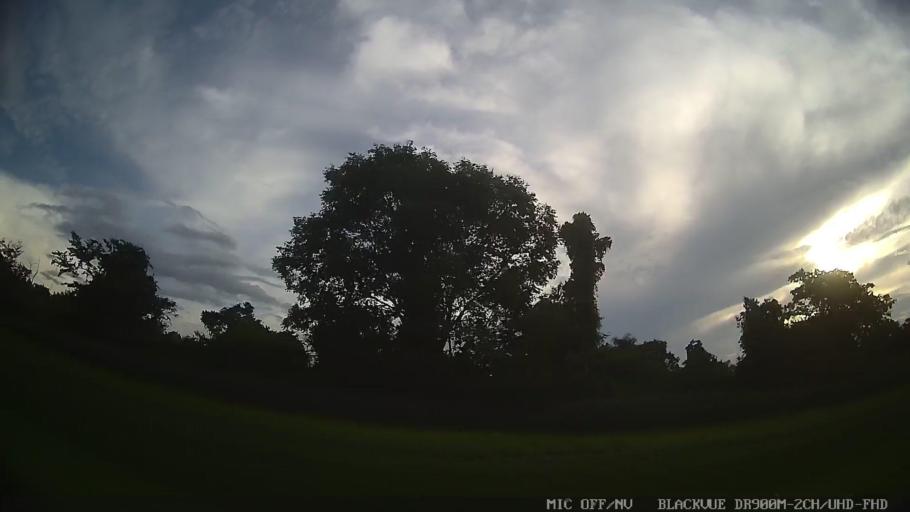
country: BR
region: Sao Paulo
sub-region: Porto Feliz
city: Porto Feliz
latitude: -23.2118
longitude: -47.5785
